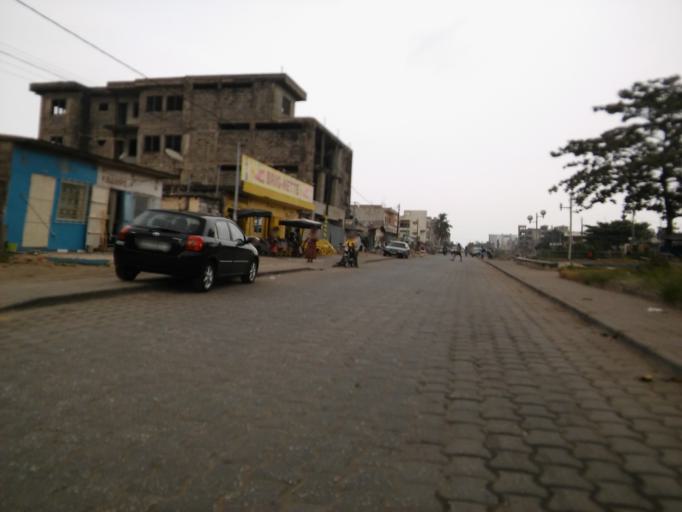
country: BJ
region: Littoral
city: Cotonou
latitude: 6.3771
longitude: 2.3962
